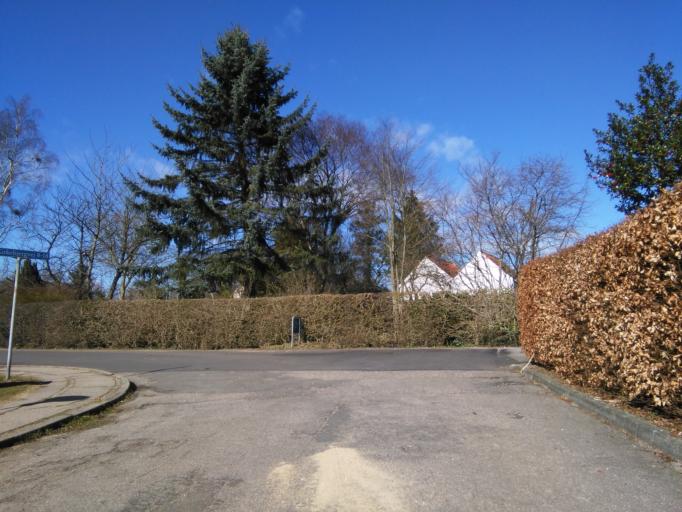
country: DK
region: Central Jutland
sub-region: Horsens Kommune
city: Horsens
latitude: 55.8920
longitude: 10.0038
